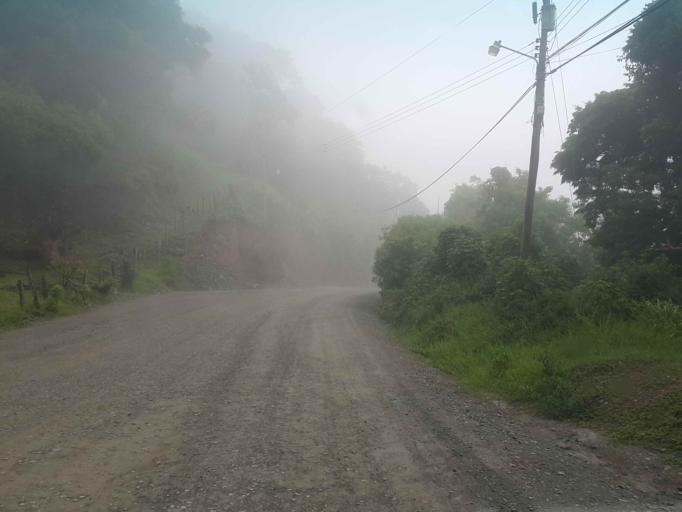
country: CR
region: Guanacaste
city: Juntas
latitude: 10.2864
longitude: -84.8349
